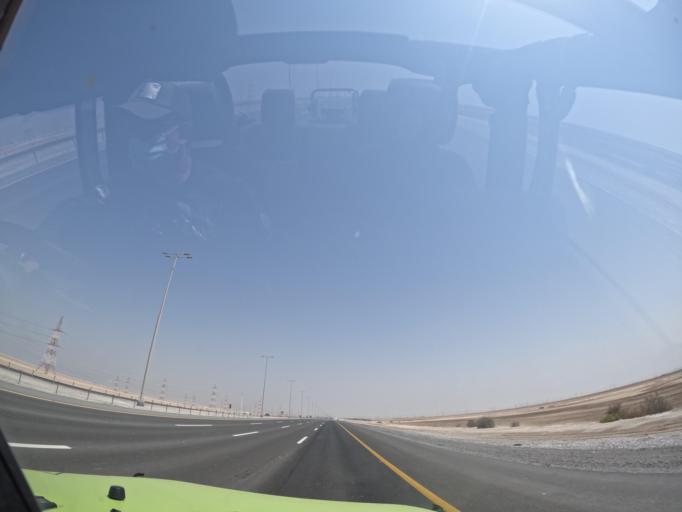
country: AE
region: Abu Dhabi
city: Abu Dhabi
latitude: 24.1541
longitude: 54.2615
